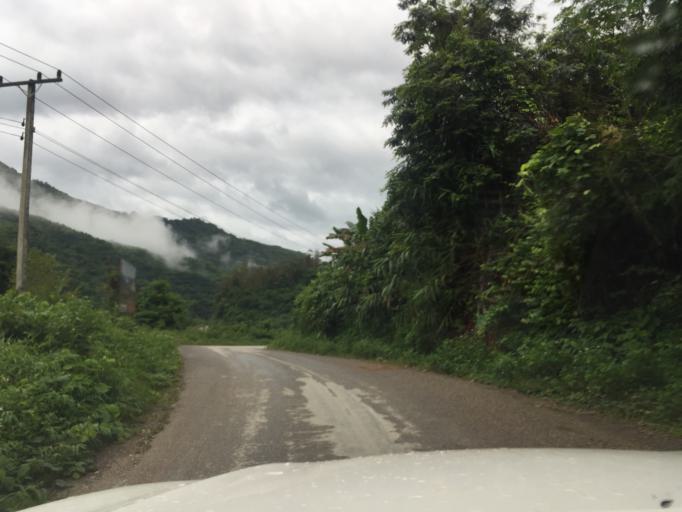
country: LA
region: Oudomxai
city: Muang La
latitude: 21.0046
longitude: 102.2327
